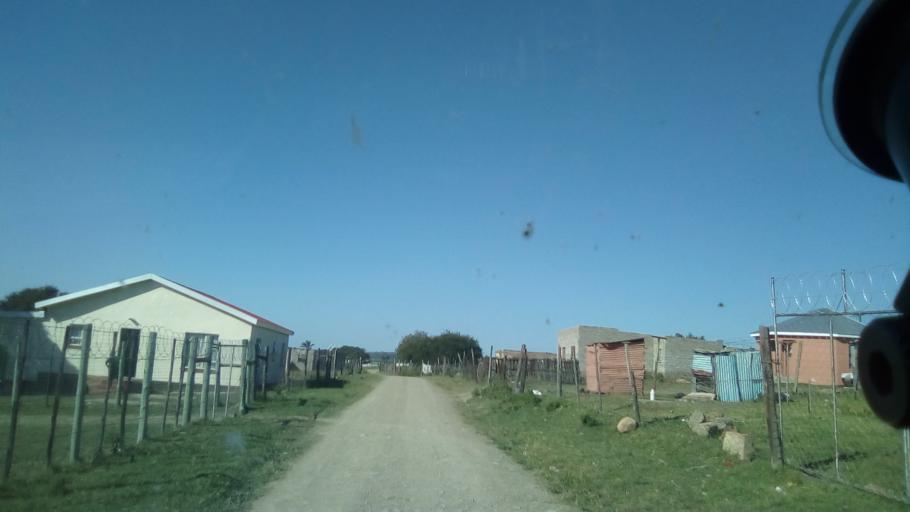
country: ZA
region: Eastern Cape
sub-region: Buffalo City Metropolitan Municipality
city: Bhisho
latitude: -32.8315
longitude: 27.3712
